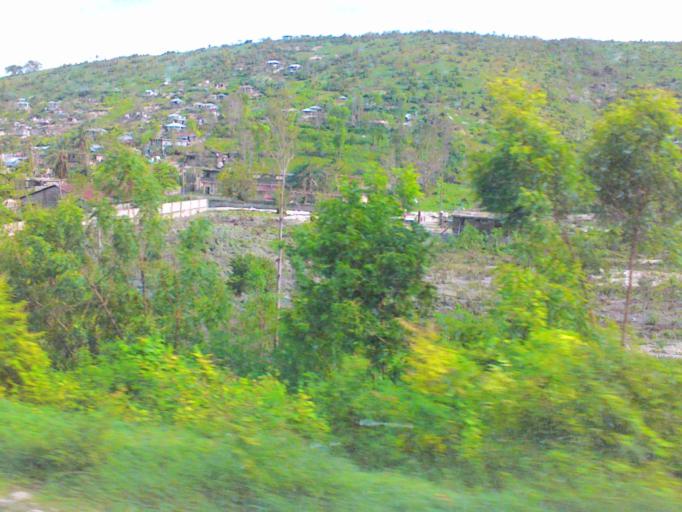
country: HT
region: Sud
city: Cavaillon
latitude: 18.2957
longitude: -73.6515
